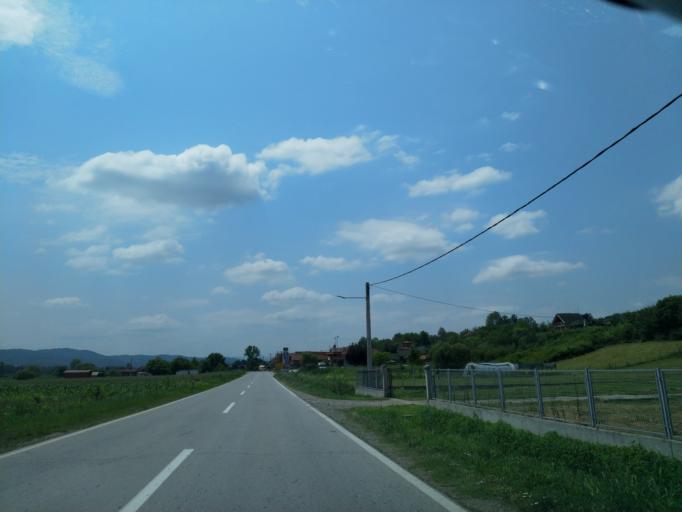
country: RS
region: Central Serbia
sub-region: Rasinski Okrug
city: Krusevac
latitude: 43.4713
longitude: 21.2572
